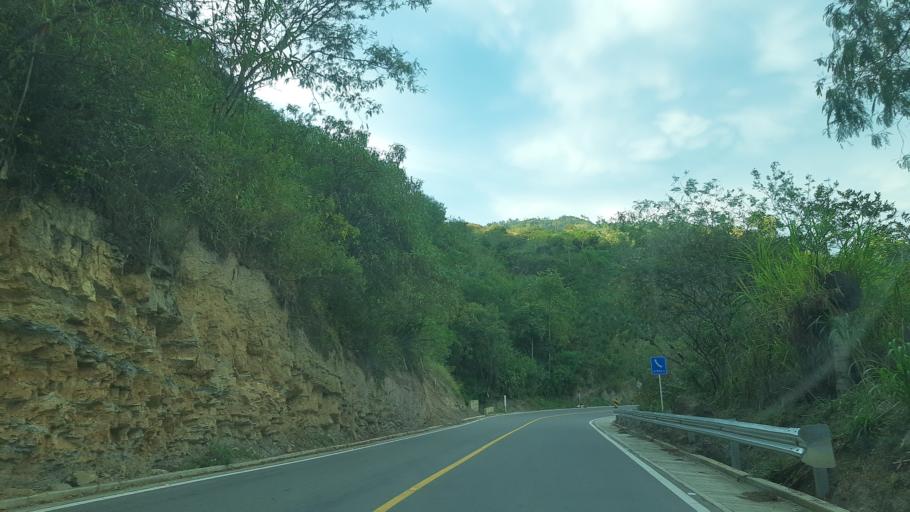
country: CO
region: Boyaca
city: Somondoco
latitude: 5.0076
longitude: -73.4412
